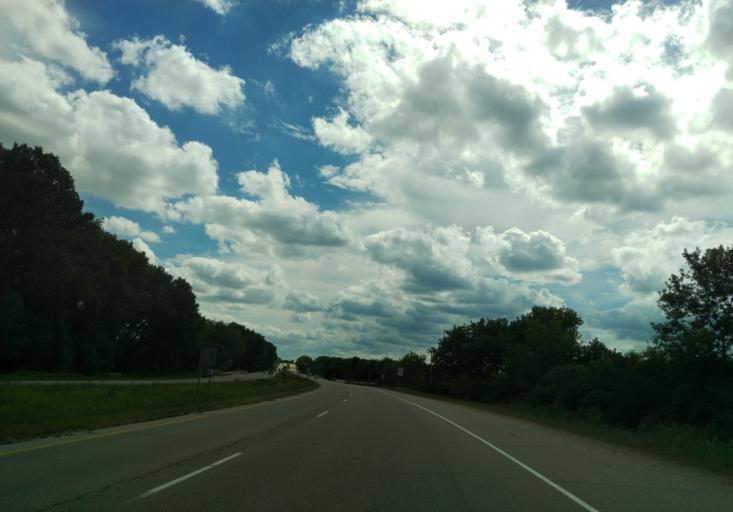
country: US
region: Wisconsin
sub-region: Dane County
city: Maple Bluff
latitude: 43.1522
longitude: -89.4034
